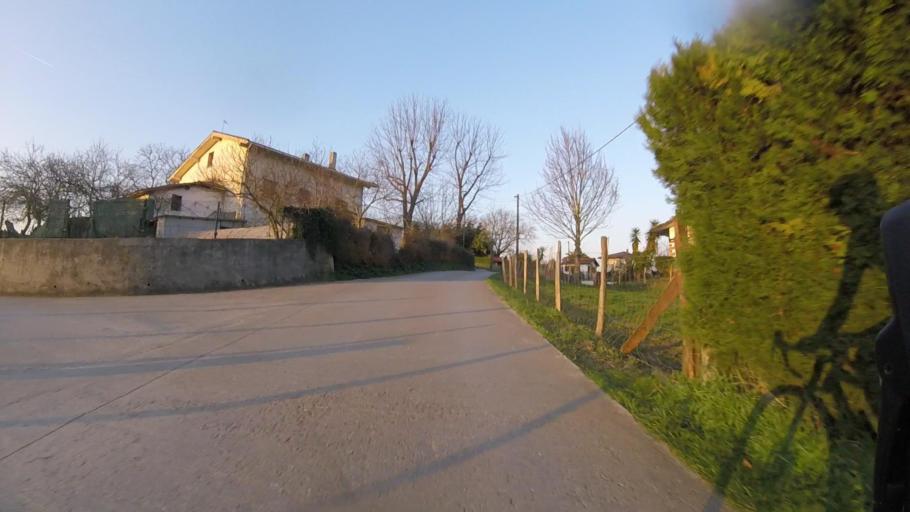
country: ES
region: Basque Country
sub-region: Provincia de Guipuzcoa
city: Errenteria
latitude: 43.2875
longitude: -1.8697
